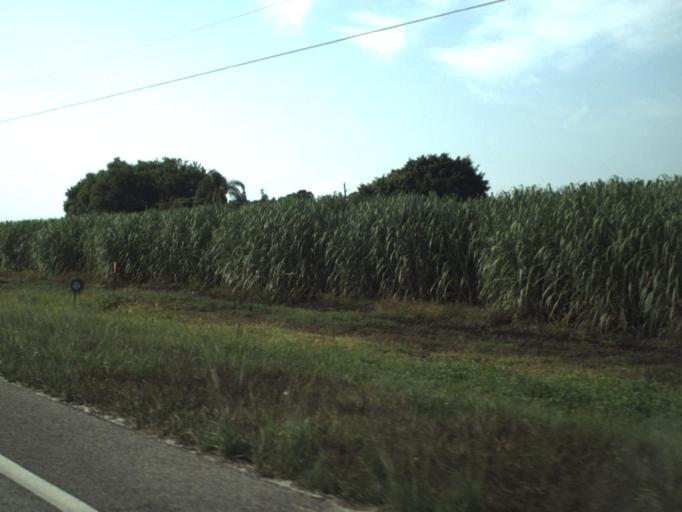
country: US
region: Florida
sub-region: Hendry County
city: Clewiston
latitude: 26.7195
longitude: -80.8436
